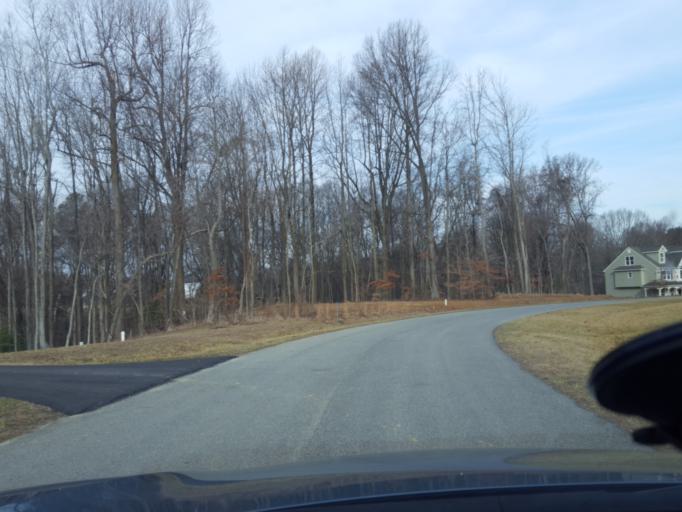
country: US
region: Maryland
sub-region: Calvert County
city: Chesapeake Beach
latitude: 38.6699
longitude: -76.5432
